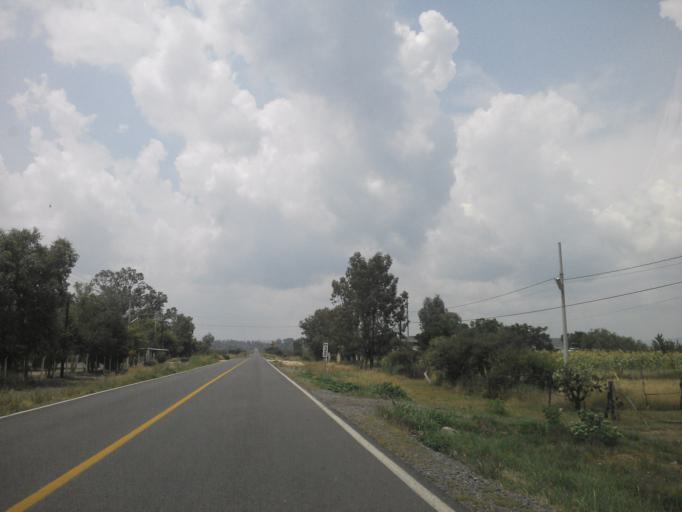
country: MX
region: Guanajuato
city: Ciudad Manuel Doblado
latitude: 20.8116
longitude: -101.9981
